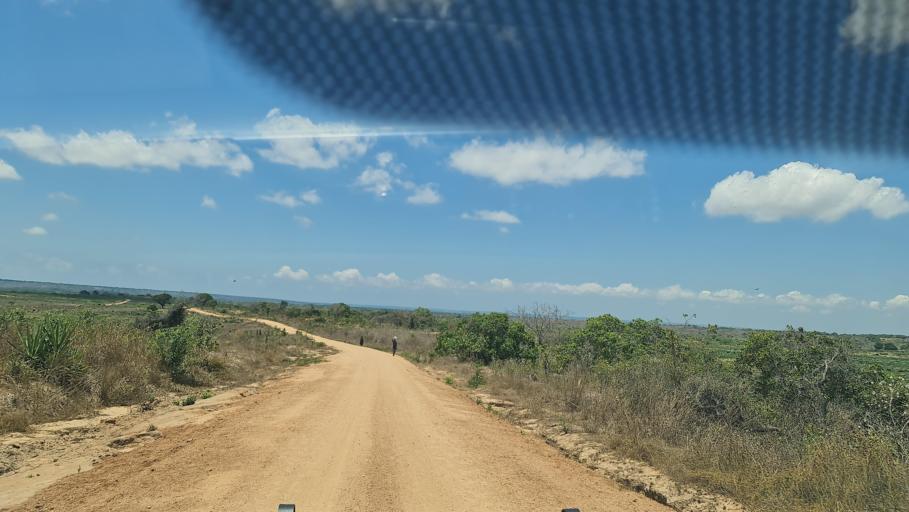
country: MZ
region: Nampula
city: Nacala
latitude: -14.3277
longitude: 40.5914
